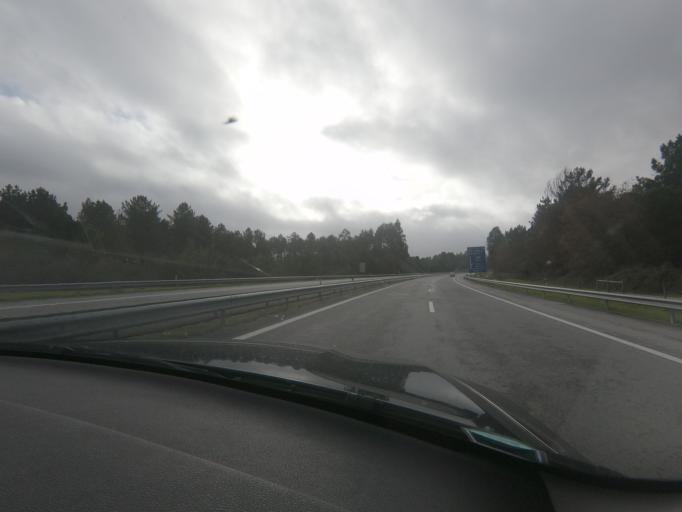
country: PT
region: Viseu
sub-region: Viseu
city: Campo
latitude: 40.7155
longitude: -7.9284
